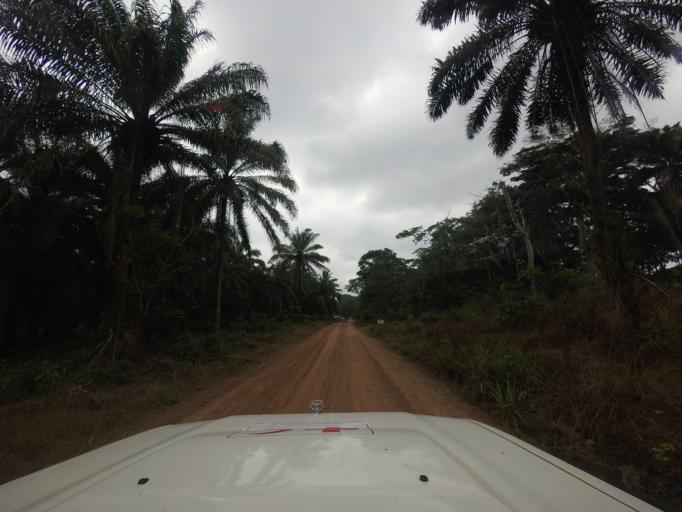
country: LR
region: Lofa
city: Voinjama
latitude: 8.4412
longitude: -9.7976
